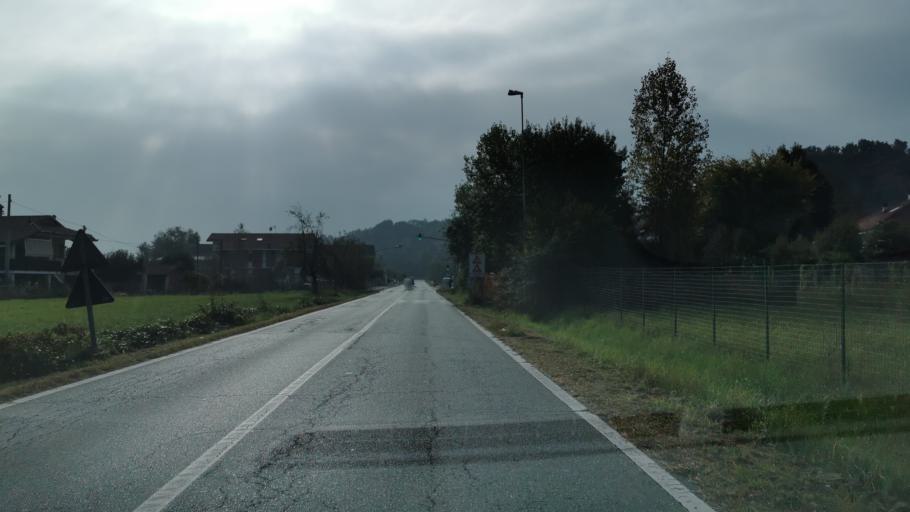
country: IT
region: Piedmont
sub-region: Provincia di Torino
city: Rivarossa
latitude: 45.2645
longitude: 7.6933
